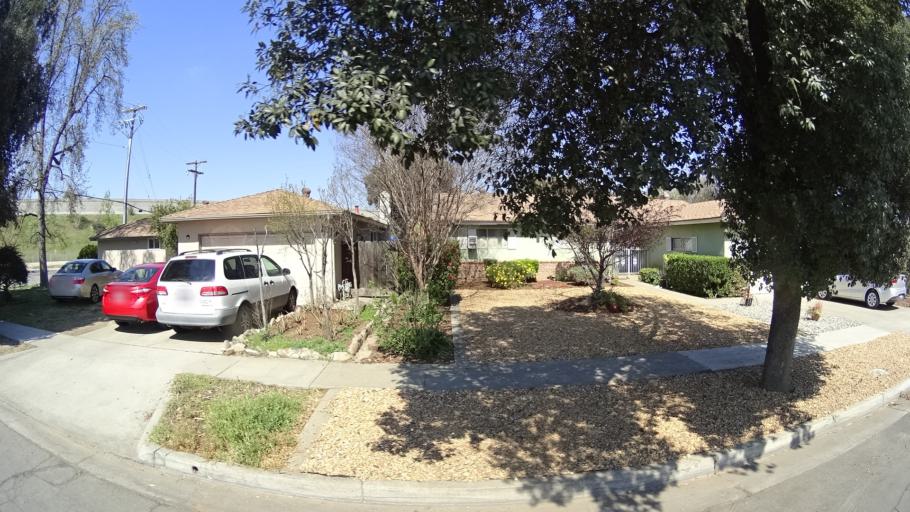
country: US
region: California
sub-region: Fresno County
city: Tarpey Village
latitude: 36.8038
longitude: -119.7359
